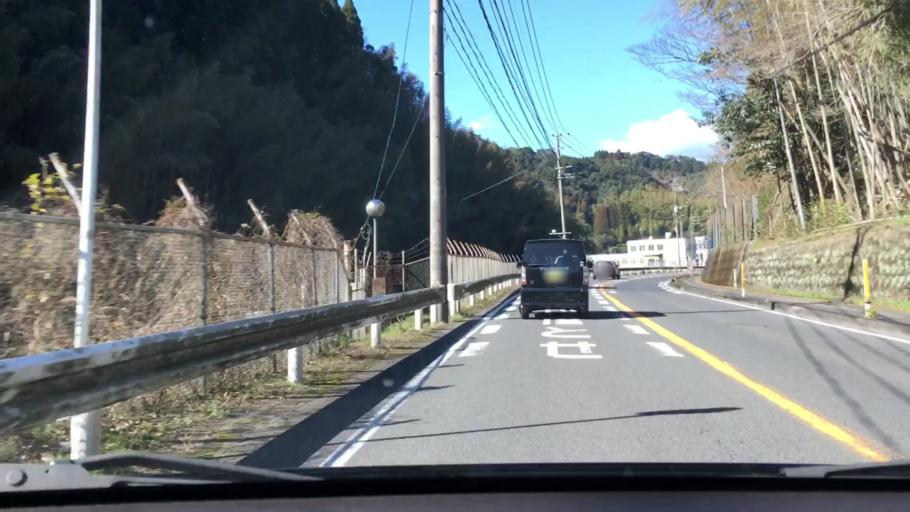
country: JP
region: Kagoshima
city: Ijuin
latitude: 31.6526
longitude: 130.4995
